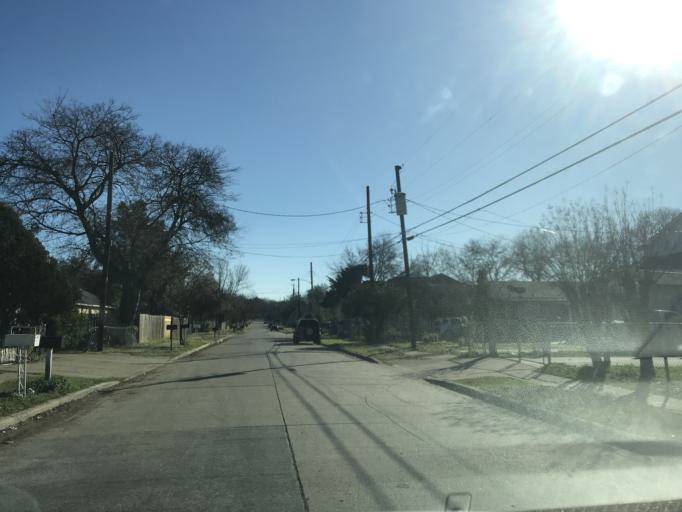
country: US
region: Texas
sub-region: Dallas County
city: Cockrell Hill
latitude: 32.7733
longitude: -96.9089
